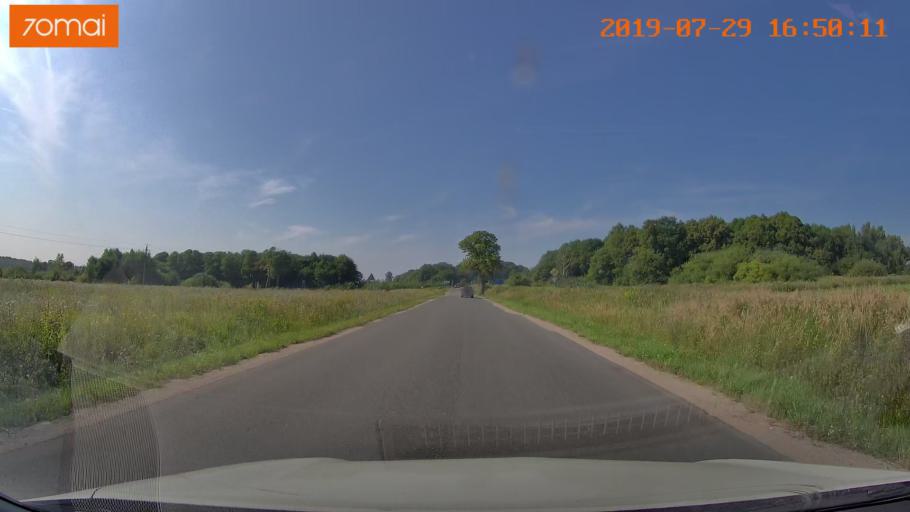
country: RU
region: Kaliningrad
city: Primorsk
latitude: 54.8011
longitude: 20.0573
